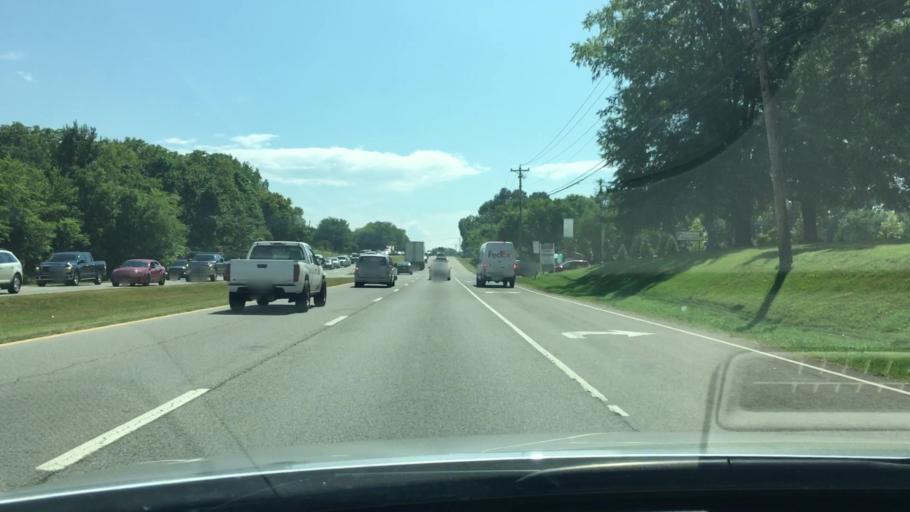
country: US
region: Tennessee
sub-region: Maury County
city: Spring Hill
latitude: 35.7009
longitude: -86.9814
